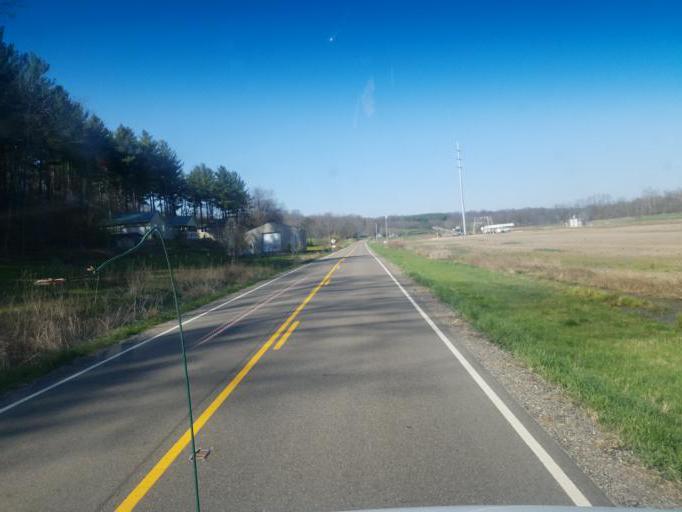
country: US
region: Ohio
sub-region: Muskingum County
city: Frazeysburg
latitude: 40.2309
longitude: -82.1610
